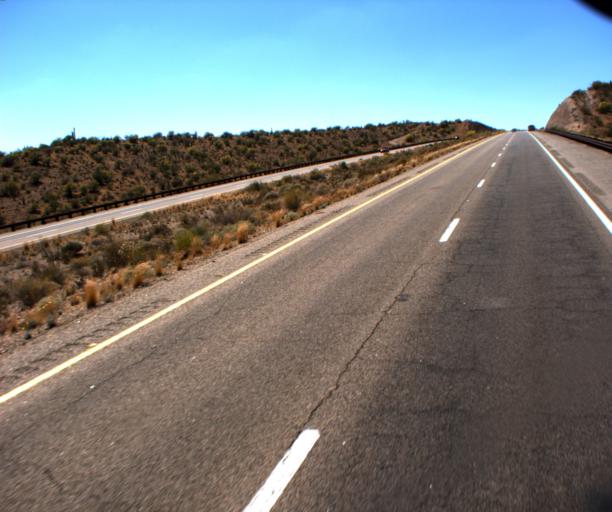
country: US
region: Arizona
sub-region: Yavapai County
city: Bagdad
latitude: 34.5840
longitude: -113.5015
